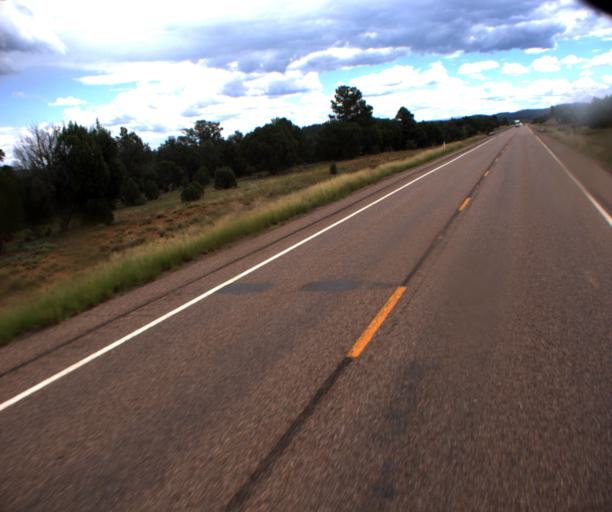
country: US
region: Arizona
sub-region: Navajo County
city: Linden
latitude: 34.3260
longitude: -110.2586
